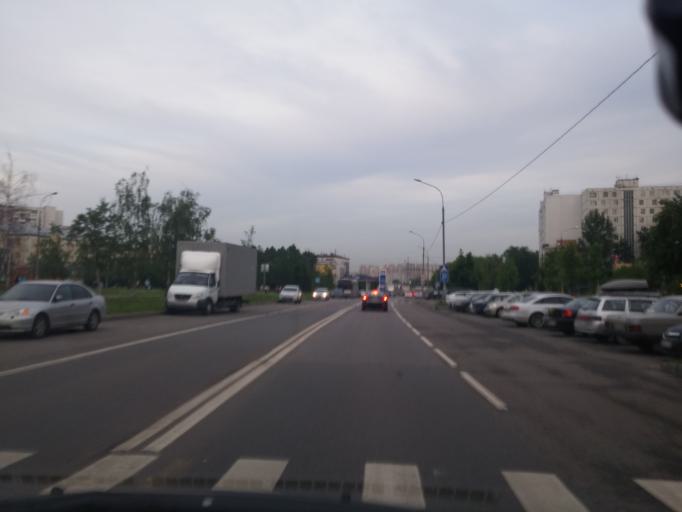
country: RU
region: Moscow
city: Bibirevo
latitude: 55.8862
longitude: 37.5973
